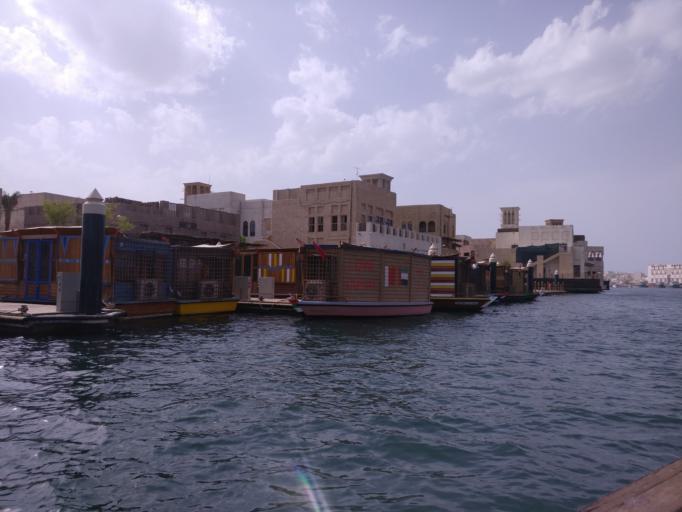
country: AE
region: Ash Shariqah
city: Sharjah
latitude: 25.2645
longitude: 55.3059
